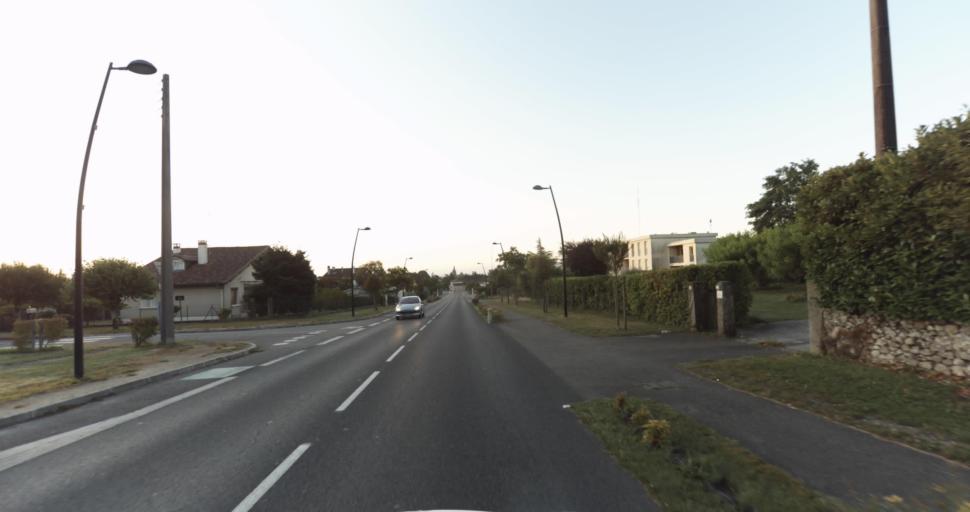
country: FR
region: Aquitaine
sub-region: Departement de la Gironde
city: Bazas
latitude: 44.4364
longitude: -0.2226
